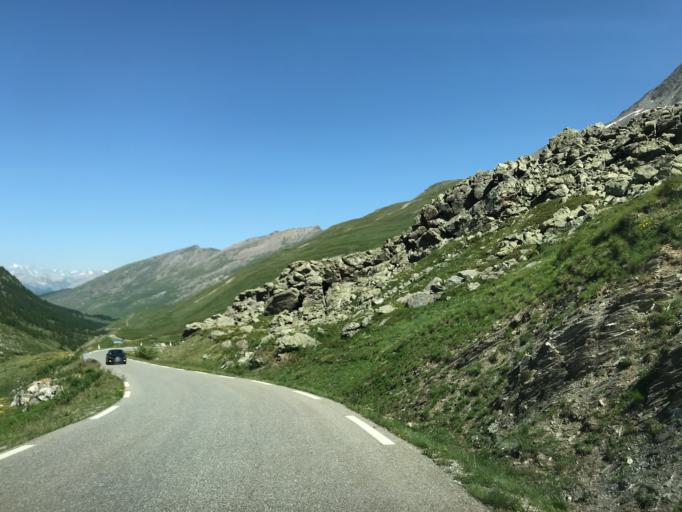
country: IT
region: Piedmont
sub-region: Provincia di Cuneo
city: Pontechianale
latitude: 44.6962
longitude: 6.9493
